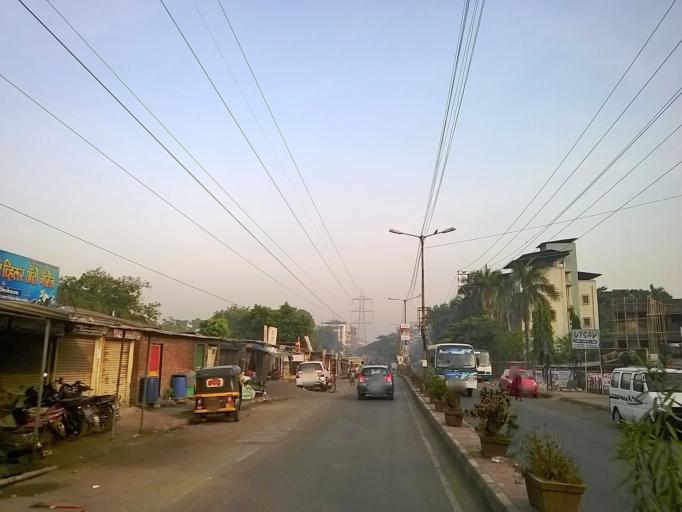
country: IN
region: Maharashtra
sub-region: Raigarh
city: Panvel
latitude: 18.9926
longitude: 73.1218
